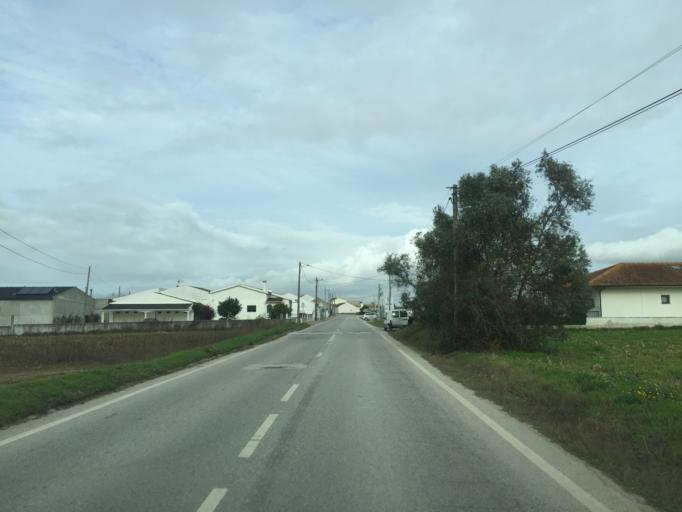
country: PT
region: Coimbra
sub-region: Figueira da Foz
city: Lavos
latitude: 40.0535
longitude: -8.8151
